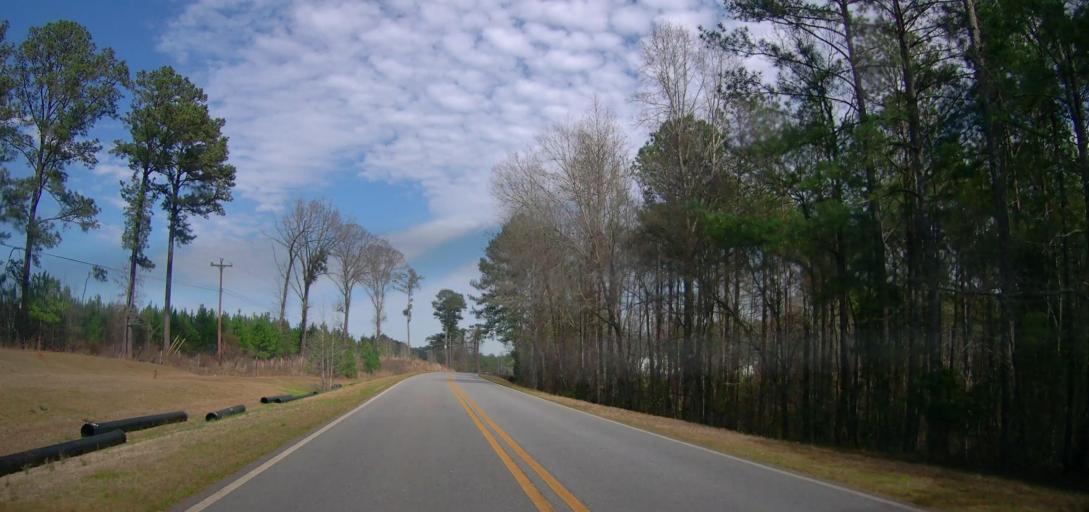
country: US
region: Georgia
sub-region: Monroe County
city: Forsyth
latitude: 33.1037
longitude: -83.8202
